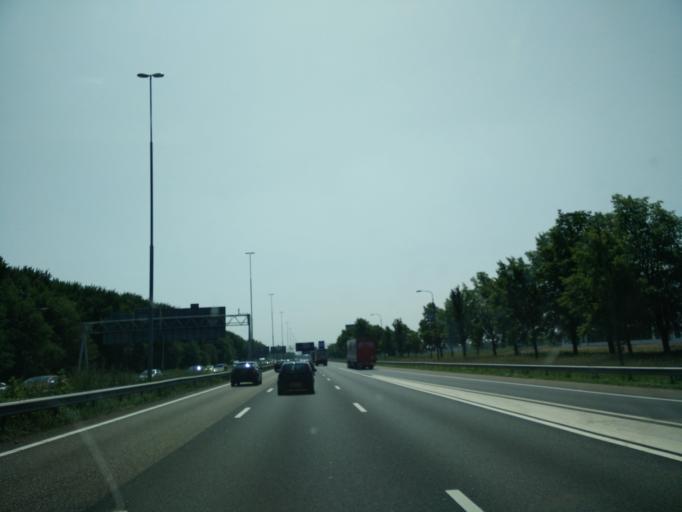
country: NL
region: South Holland
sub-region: Gemeente Delft
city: Delft
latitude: 51.9919
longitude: 4.3909
